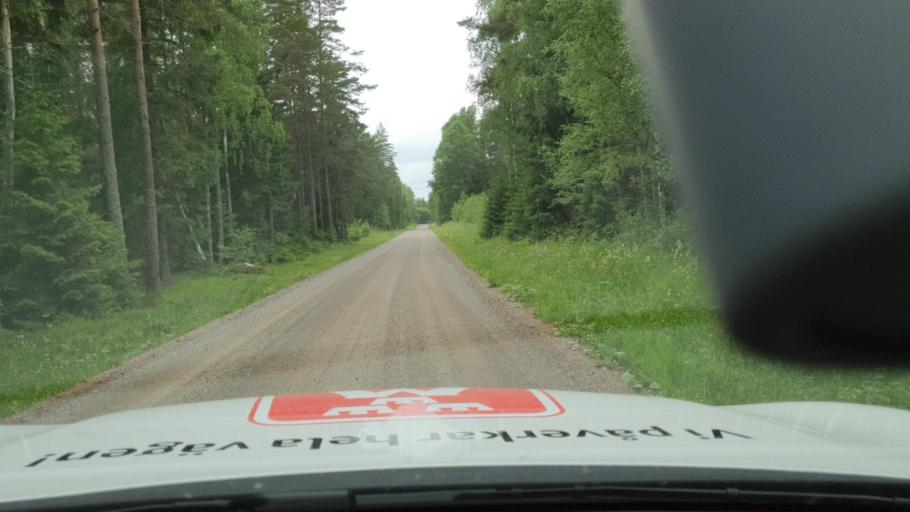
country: SE
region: Vaestra Goetaland
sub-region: Tidaholms Kommun
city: Tidaholm
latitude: 58.1602
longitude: 14.0462
